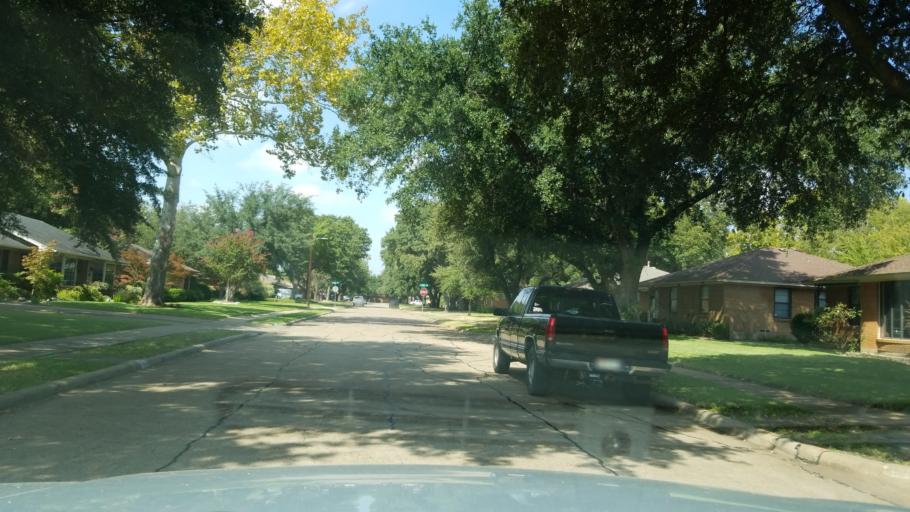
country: US
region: Texas
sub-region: Dallas County
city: Garland
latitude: 32.8957
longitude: -96.6621
